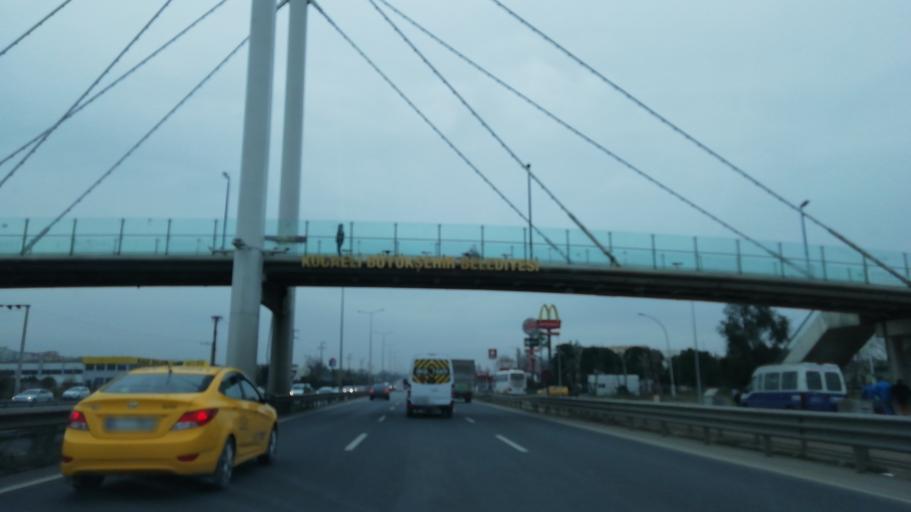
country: TR
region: Kocaeli
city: Darica
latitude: 40.8115
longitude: 29.3683
